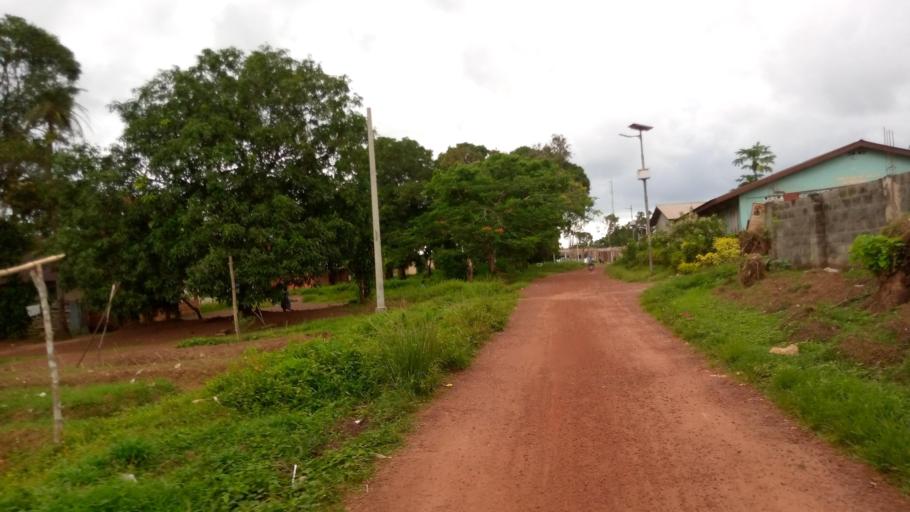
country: SL
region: Southern Province
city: Moyamba
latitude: 8.1634
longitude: -12.4389
